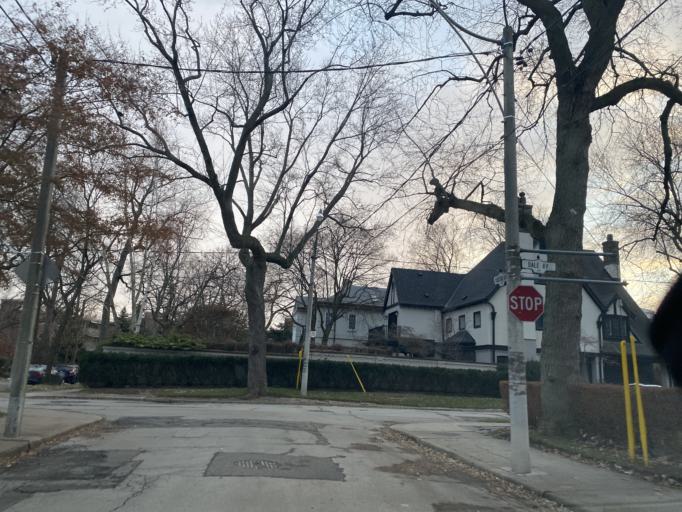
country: CA
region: Ontario
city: Toronto
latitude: 43.6748
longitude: -79.3715
